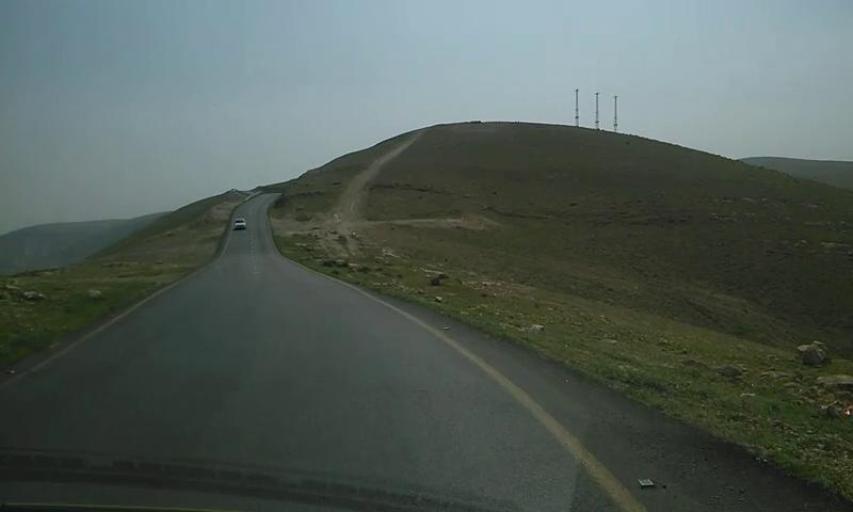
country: PS
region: West Bank
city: Rammun
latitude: 31.9127
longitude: 35.3613
